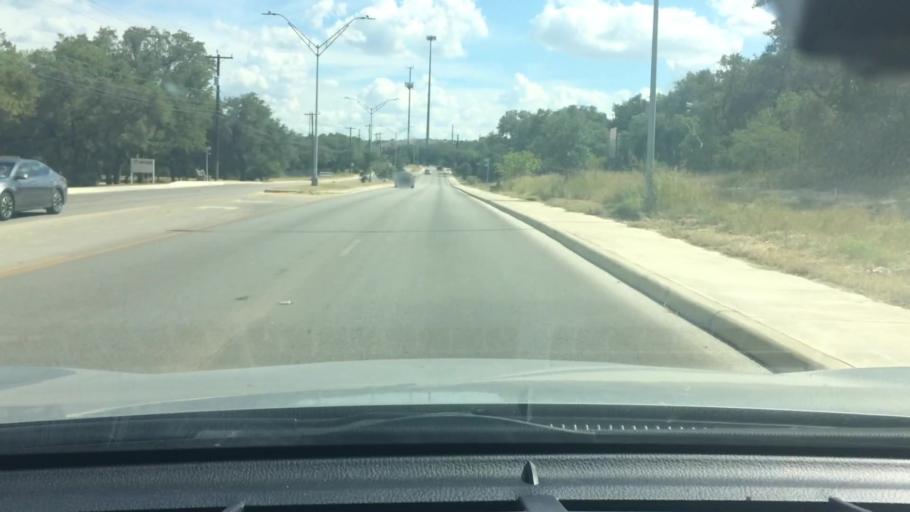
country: US
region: Texas
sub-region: Bexar County
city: Leon Valley
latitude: 29.4857
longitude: -98.7003
